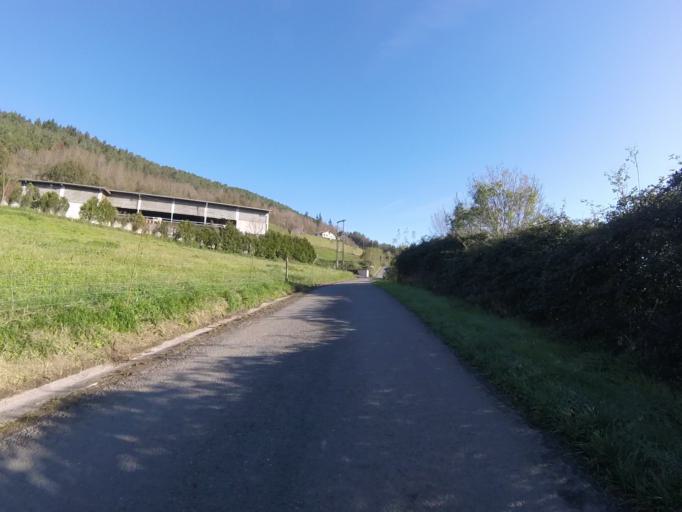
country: ES
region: Basque Country
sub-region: Provincia de Guipuzcoa
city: Usurbil
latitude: 43.2880
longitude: -2.0650
